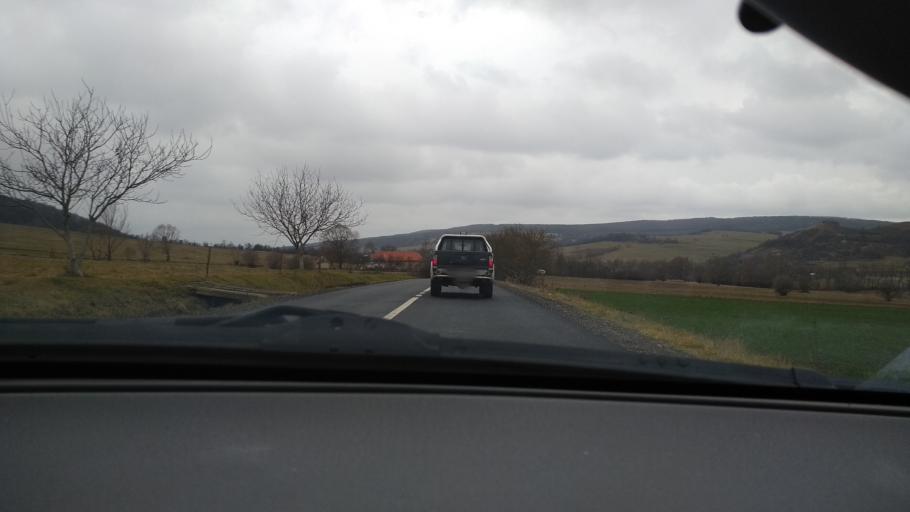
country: RO
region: Mures
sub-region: Comuna Bereni
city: Bereni
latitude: 46.5584
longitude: 24.8777
